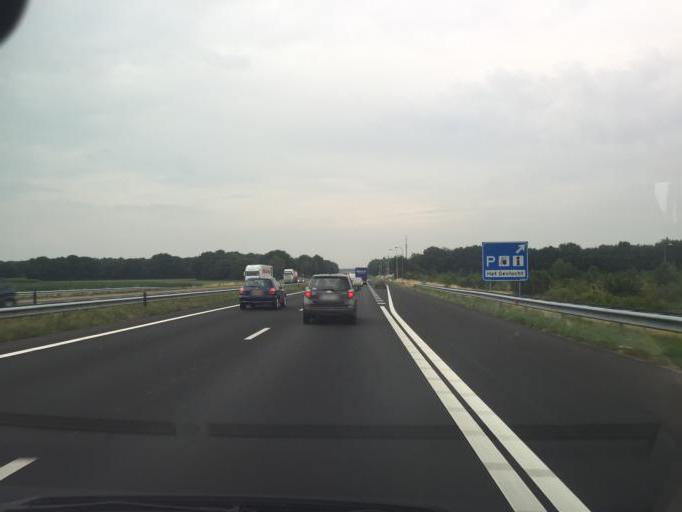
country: NL
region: North Brabant
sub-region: Gemeente Asten
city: Asten
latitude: 51.4065
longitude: 5.8061
